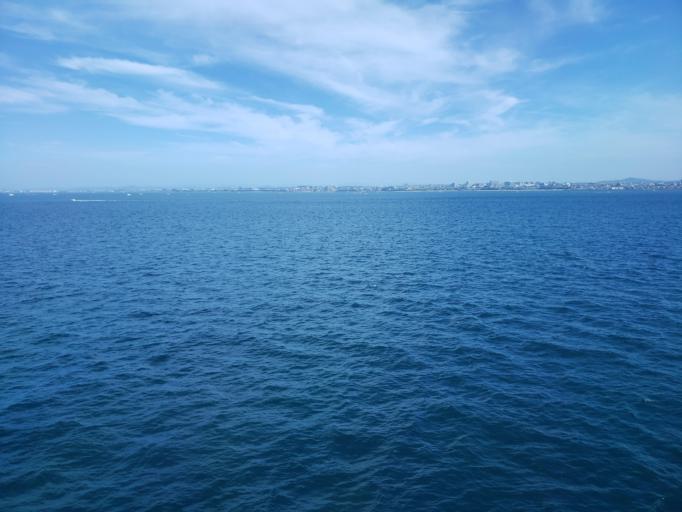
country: JP
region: Hyogo
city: Akashi
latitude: 34.6213
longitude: 134.9591
